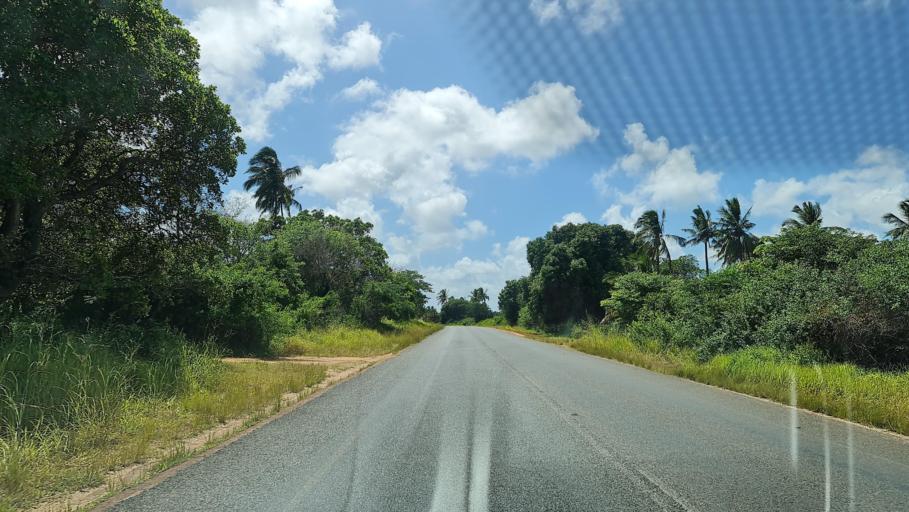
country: MZ
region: Inhambane
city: Maxixe
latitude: -24.5401
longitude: 34.9310
